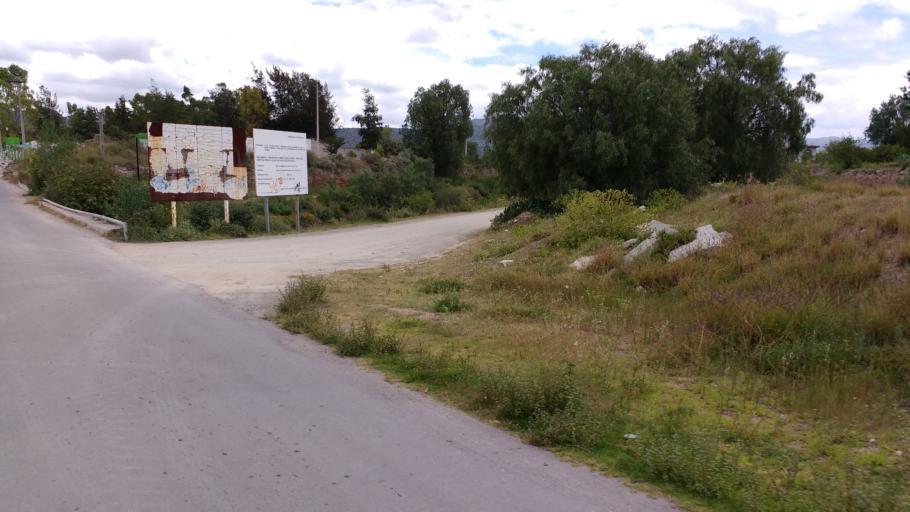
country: MX
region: Hidalgo
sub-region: Tezontepec de Aldama
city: Tenango
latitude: 20.2272
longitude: -99.2561
